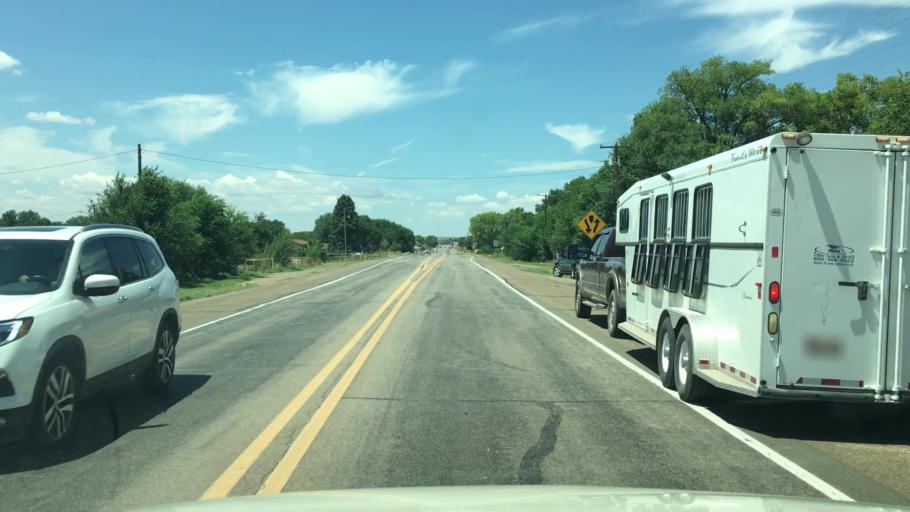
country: US
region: New Mexico
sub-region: De Baca County
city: Fort Sumner
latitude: 34.4643
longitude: -104.2223
